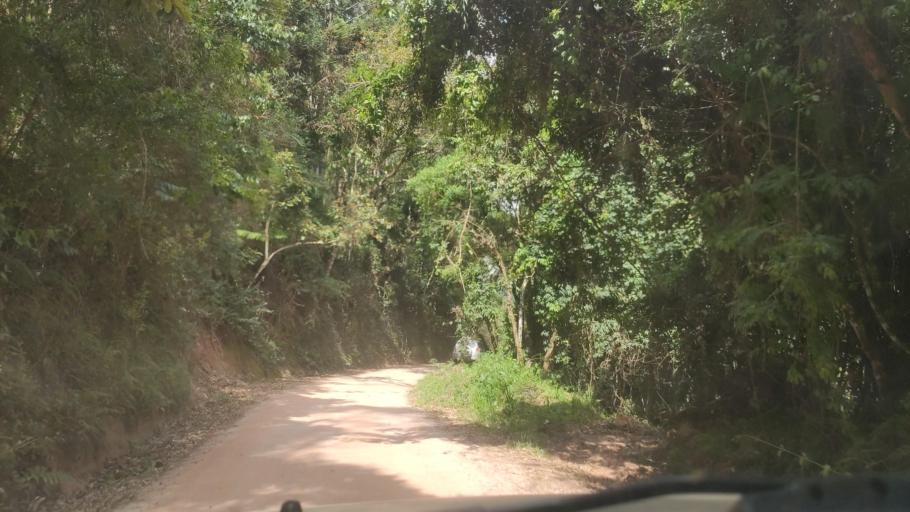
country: BR
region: Minas Gerais
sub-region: Camanducaia
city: Camanducaia
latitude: -22.7708
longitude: -46.0047
